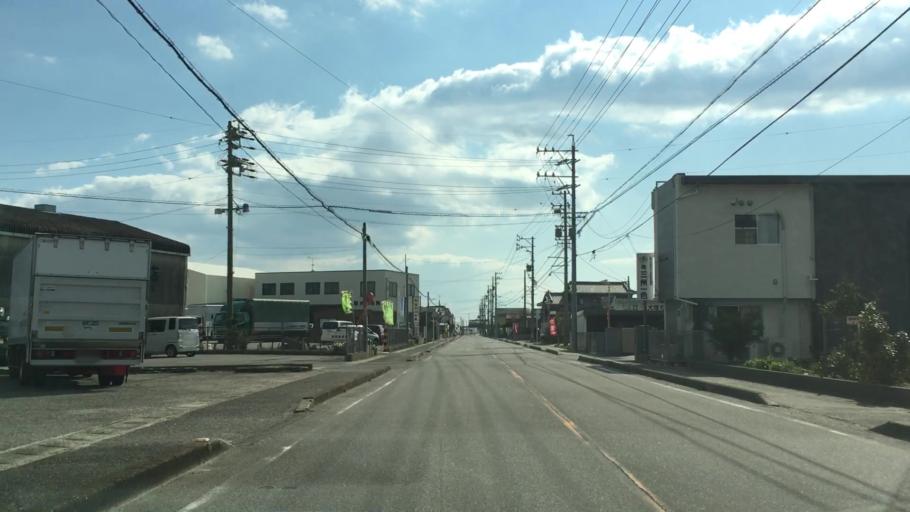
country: JP
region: Aichi
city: Ishiki
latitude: 34.7893
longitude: 137.0335
